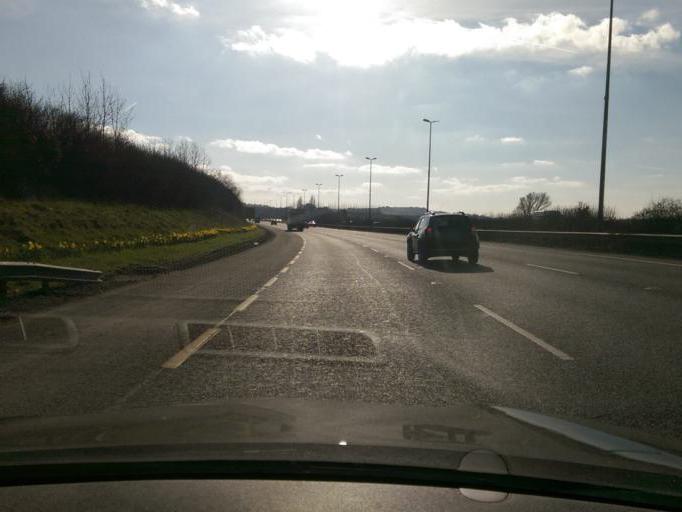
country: IE
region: Leinster
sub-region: South Dublin
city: Saggart
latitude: 53.2900
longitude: -6.4469
